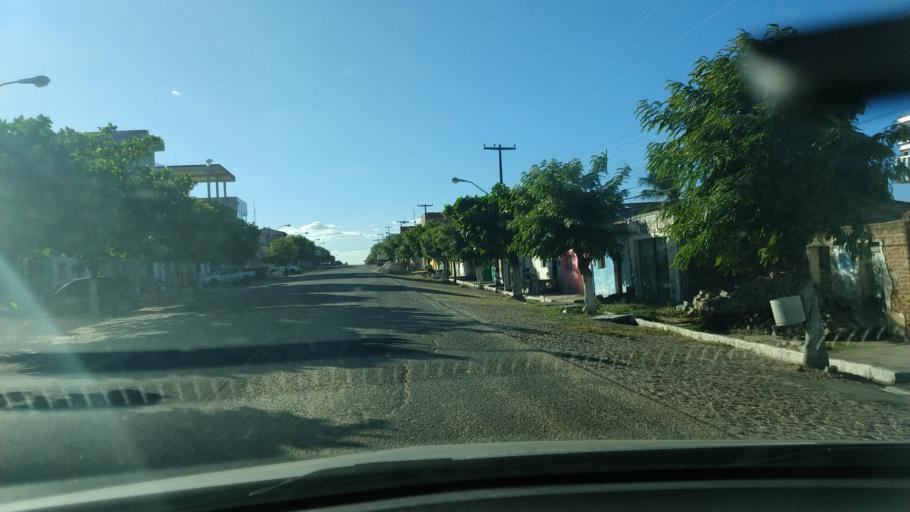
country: BR
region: Rio Grande do Norte
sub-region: Sao Jose Do Campestre
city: Sao Jose do Campestre
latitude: -6.4378
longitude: -35.6428
